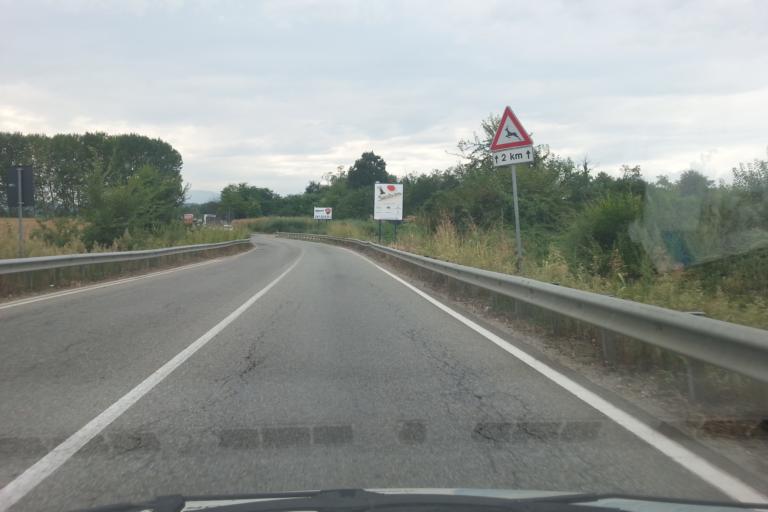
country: IT
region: Piedmont
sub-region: Provincia di Torino
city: Pasta
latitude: 45.0265
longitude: 7.5502
